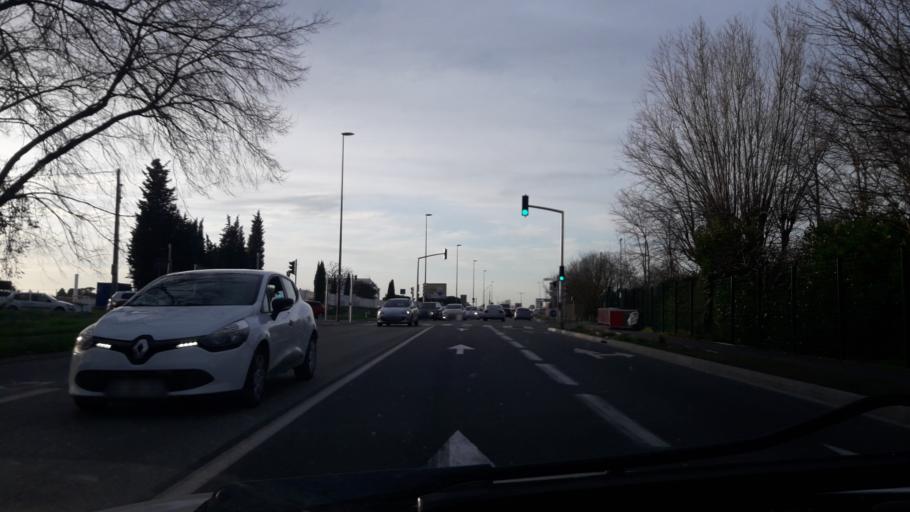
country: FR
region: Midi-Pyrenees
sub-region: Departement de la Haute-Garonne
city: Portet-sur-Garonne
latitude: 43.5596
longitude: 1.3957
